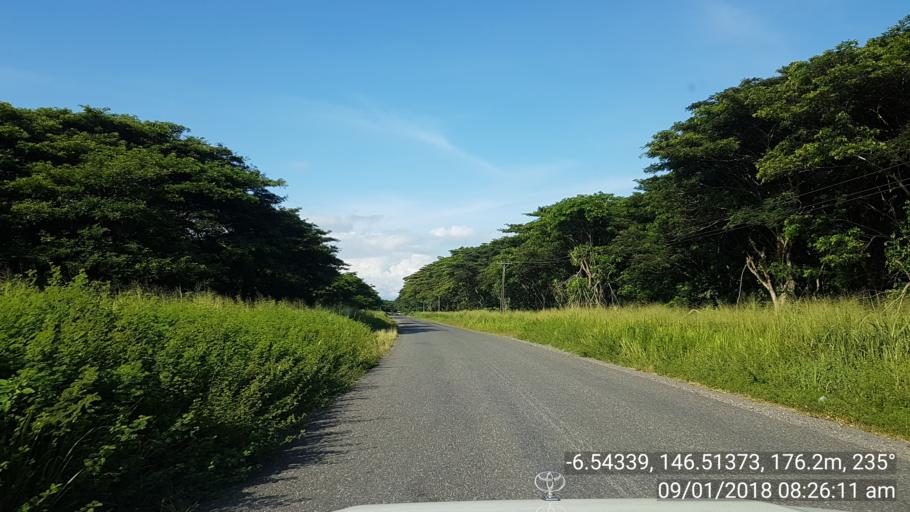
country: PG
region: Morobe
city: Lae
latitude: -6.5433
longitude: 146.5137
